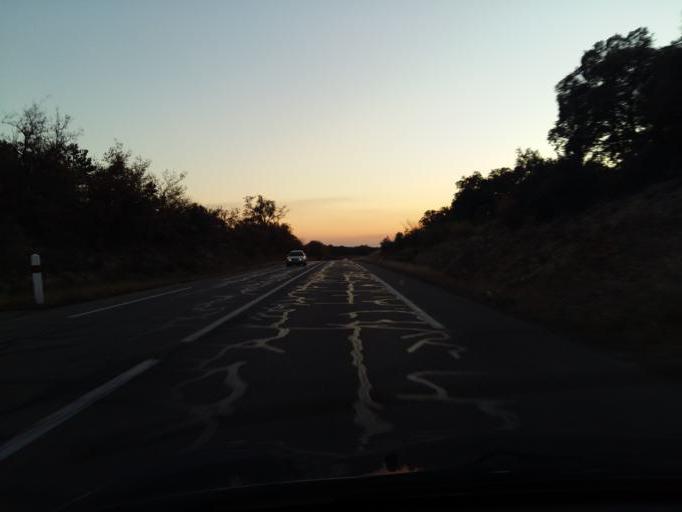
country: FR
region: Provence-Alpes-Cote d'Azur
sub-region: Departement du Vaucluse
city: Visan
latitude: 44.3479
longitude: 4.9555
